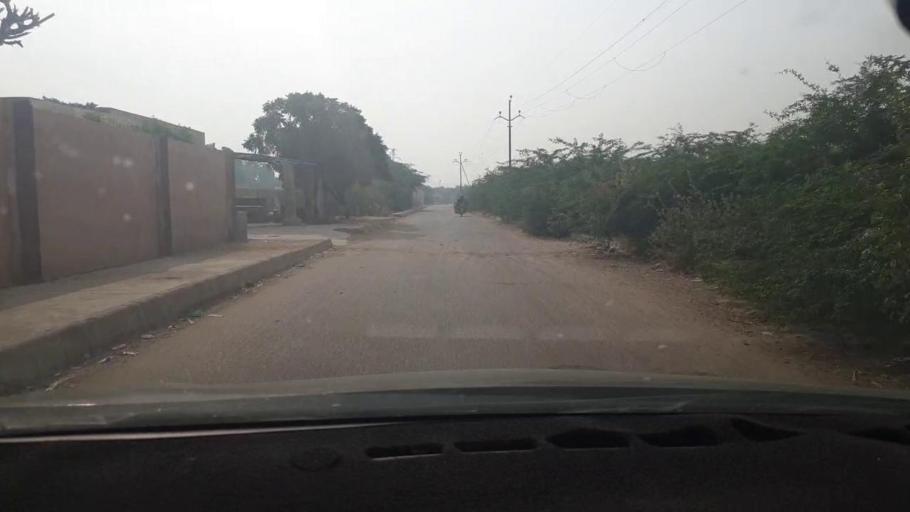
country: PK
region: Sindh
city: Malir Cantonment
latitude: 24.9363
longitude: 67.3348
